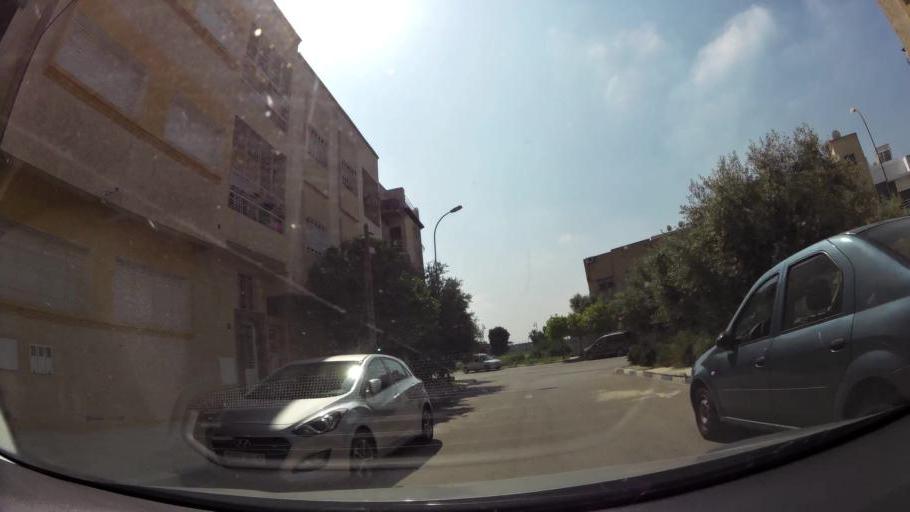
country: MA
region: Fes-Boulemane
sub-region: Fes
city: Fes
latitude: 34.0544
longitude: -5.0242
